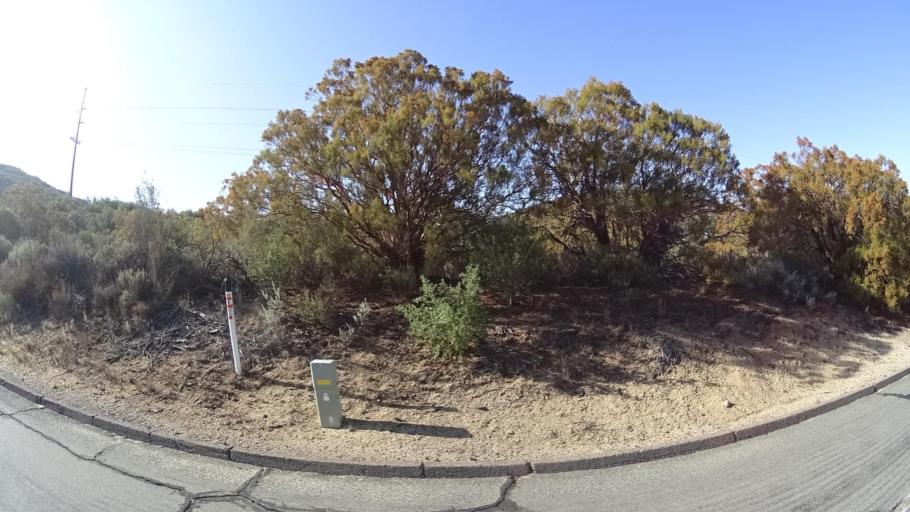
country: US
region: California
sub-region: San Diego County
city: Pine Valley
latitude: 32.8181
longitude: -116.5233
